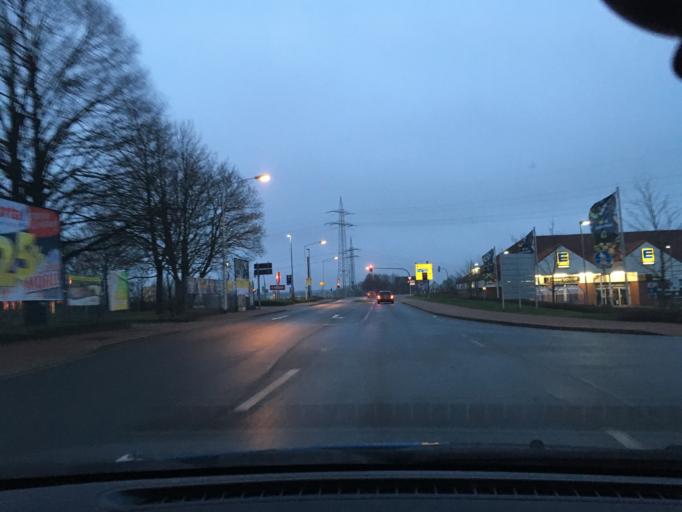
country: DE
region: Lower Saxony
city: Lehrte
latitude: 52.3599
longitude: 9.9122
